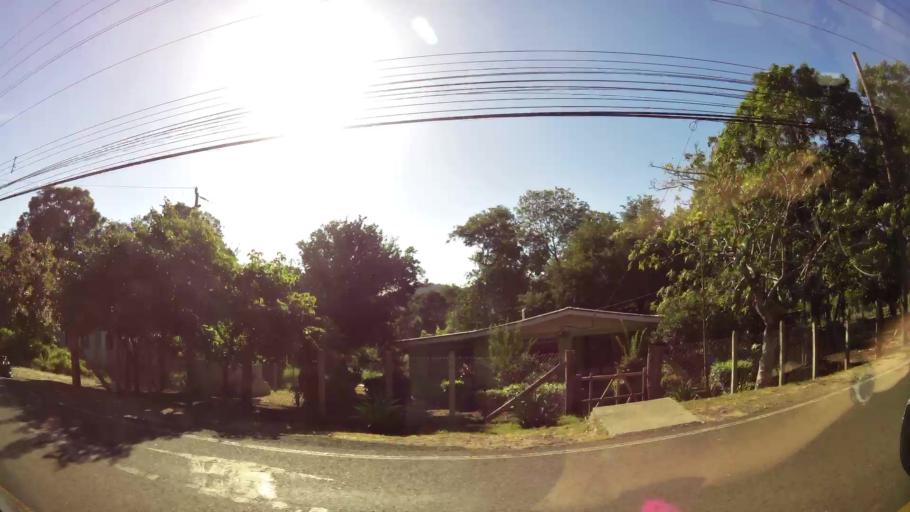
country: CR
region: Guanacaste
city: Belen
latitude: 10.3926
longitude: -85.6148
